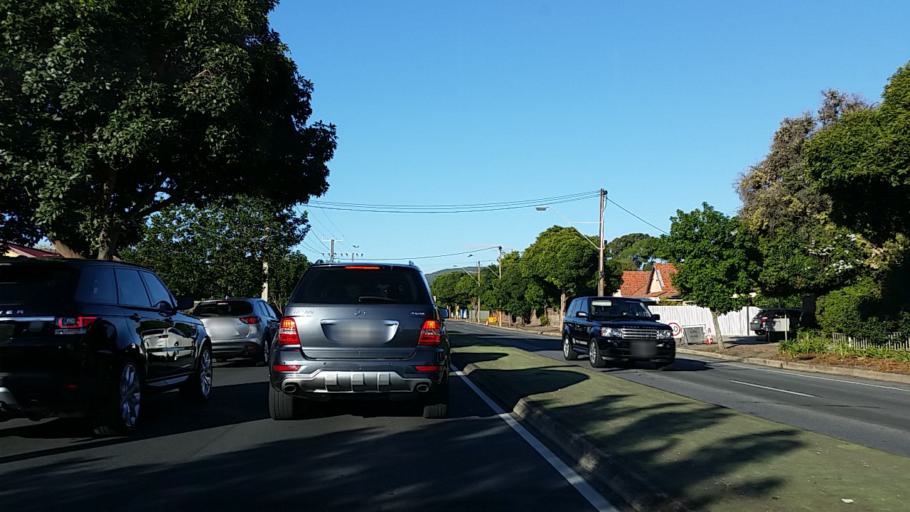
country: AU
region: South Australia
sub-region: Burnside
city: Glenunga
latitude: -34.9395
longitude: 138.6374
